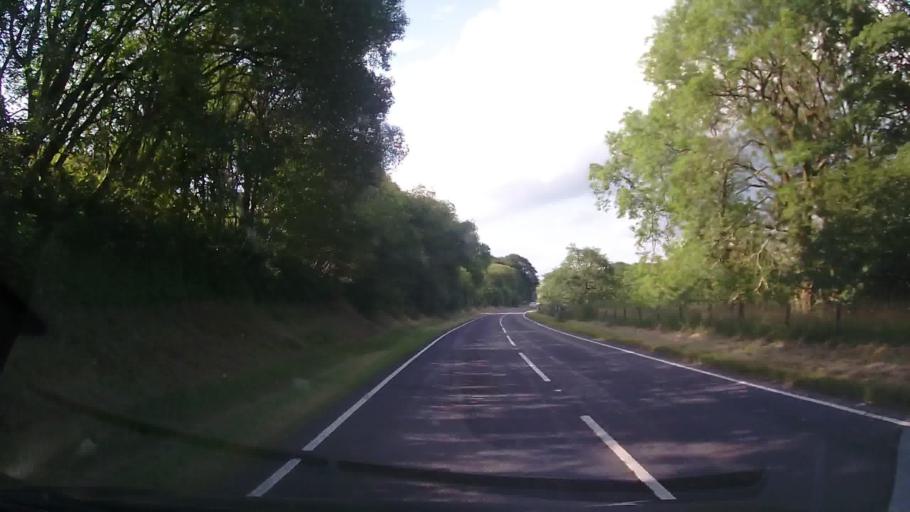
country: GB
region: Wales
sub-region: Gwynedd
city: Bala
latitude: 52.9555
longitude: -3.7208
